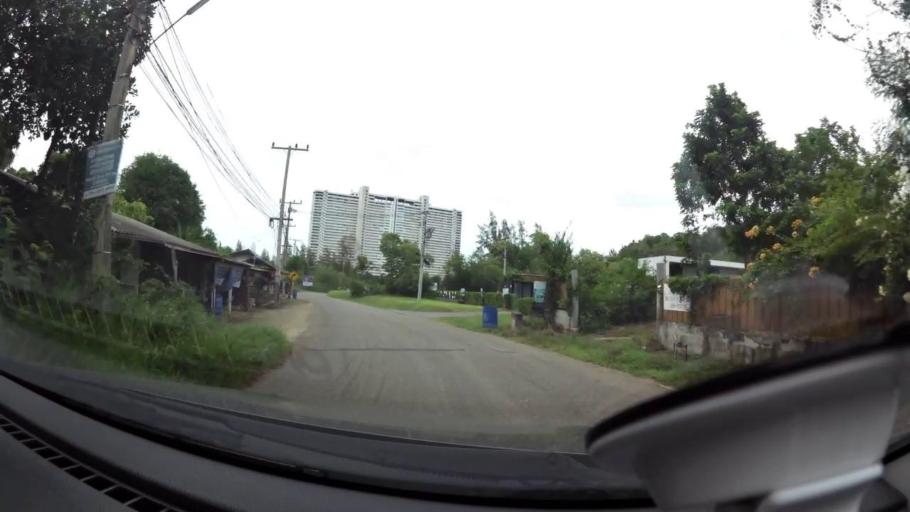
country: TH
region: Prachuap Khiri Khan
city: Pran Buri
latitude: 12.4351
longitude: 99.9753
